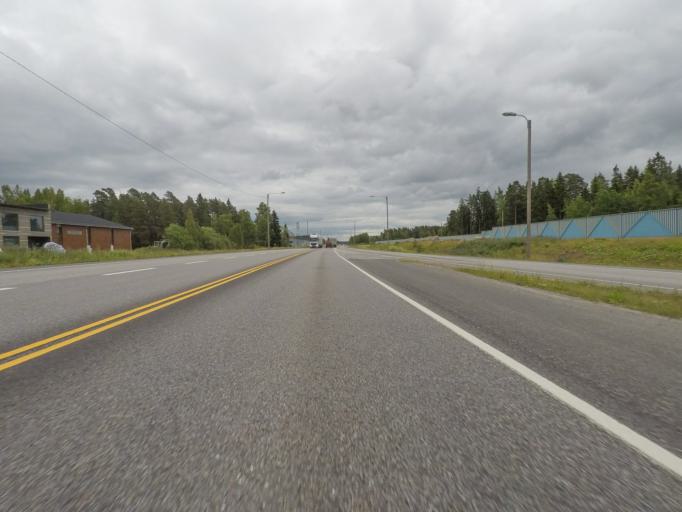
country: FI
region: Varsinais-Suomi
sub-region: Turku
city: Lieto
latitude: 60.4633
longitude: 22.4190
